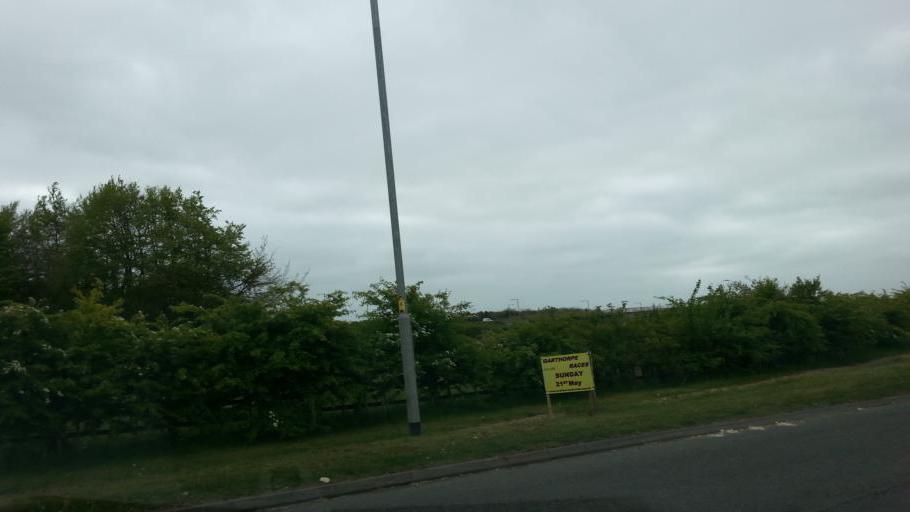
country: GB
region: England
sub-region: District of Rutland
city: Clipsham
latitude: 52.8034
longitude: -0.6129
